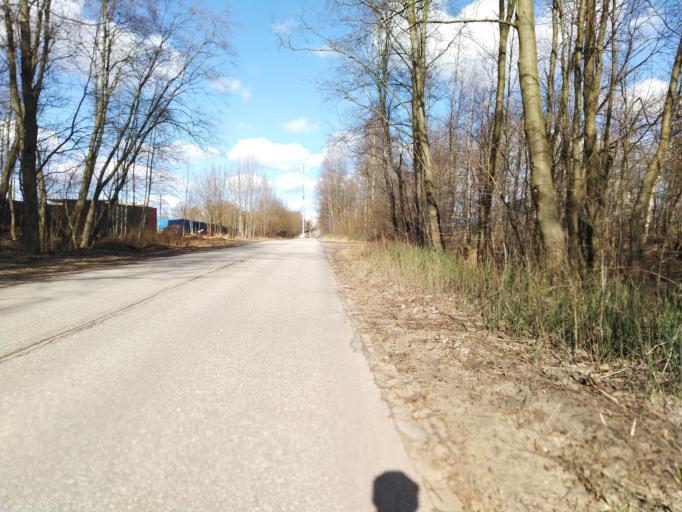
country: RU
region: Leningrad
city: Novoye Devyatkino
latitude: 60.1035
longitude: 30.4801
